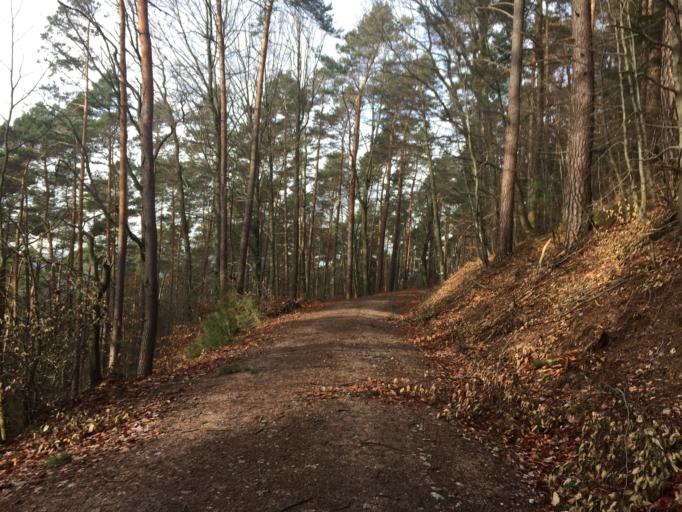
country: DE
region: Hesse
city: Reichelsheim
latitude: 49.6963
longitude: 8.8935
